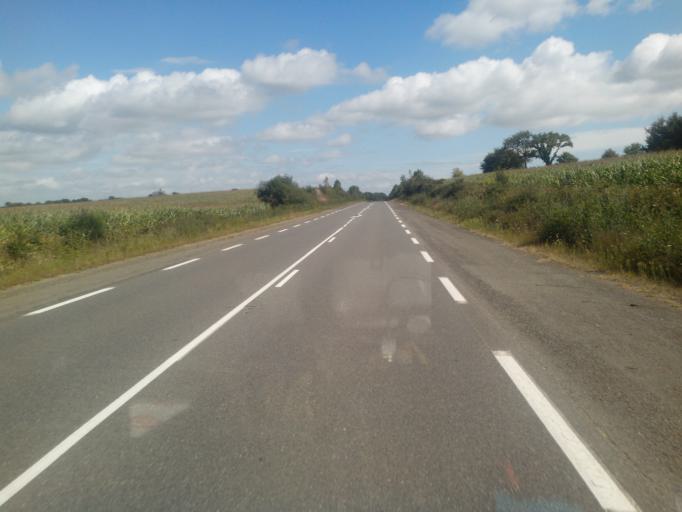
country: FR
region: Brittany
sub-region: Departement du Morbihan
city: Limerzel
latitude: 47.6158
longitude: -2.3994
